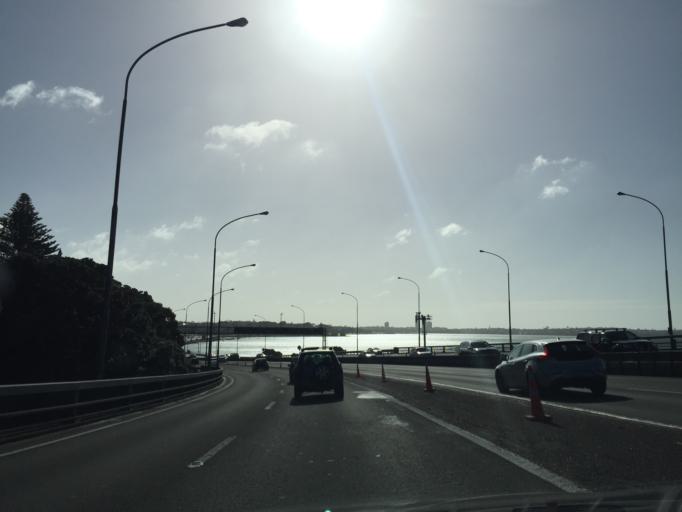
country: NZ
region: Auckland
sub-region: Auckland
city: North Shore
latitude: -36.8239
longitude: 174.7500
